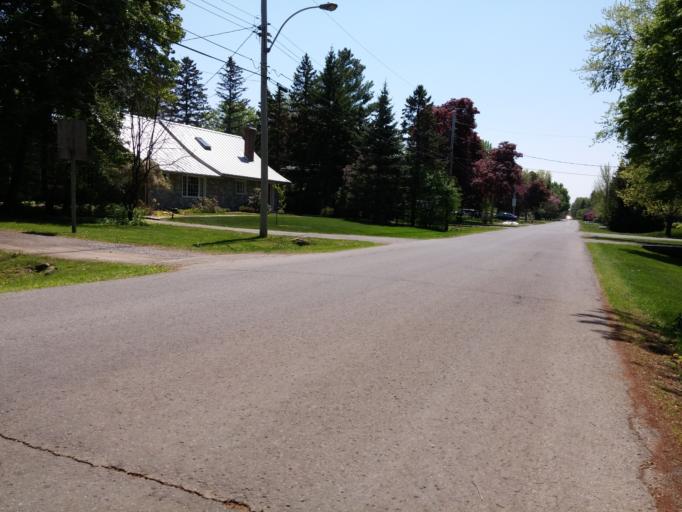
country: CA
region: Quebec
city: Baie-D'Urfe
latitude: 45.4201
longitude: -73.8980
